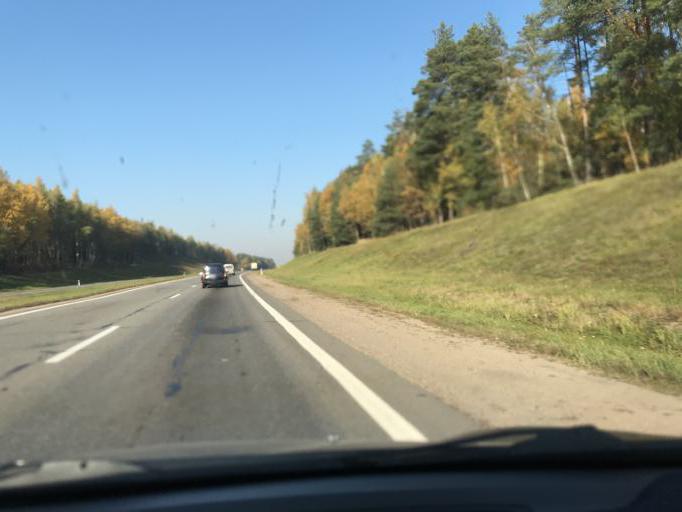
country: BY
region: Minsk
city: Luhavaya Slabada
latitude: 53.7635
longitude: 27.8284
